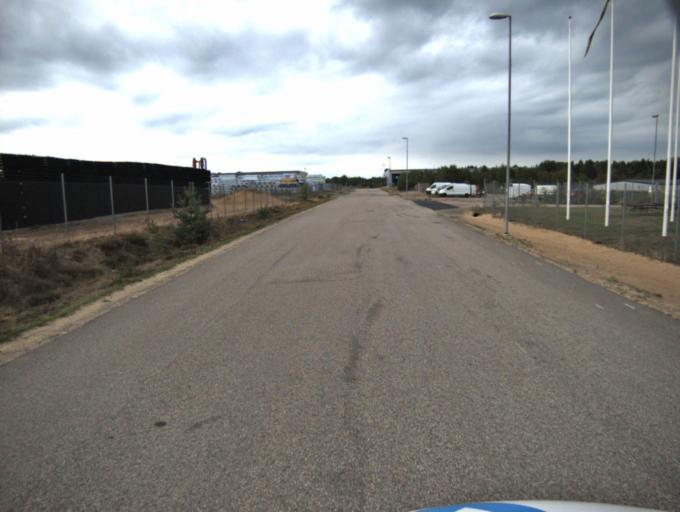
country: SE
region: Vaestra Goetaland
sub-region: Ulricehamns Kommun
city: Ulricehamn
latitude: 57.8367
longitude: 13.4230
